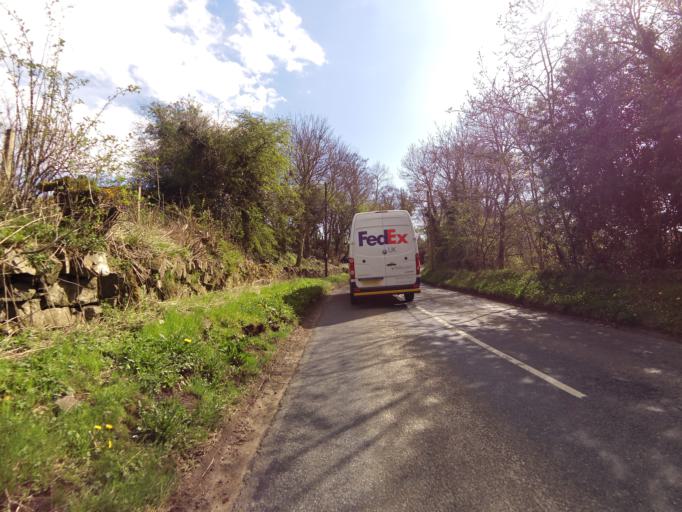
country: GB
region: Scotland
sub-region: Fife
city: Auchtermuchty
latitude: 56.3008
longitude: -3.2389
